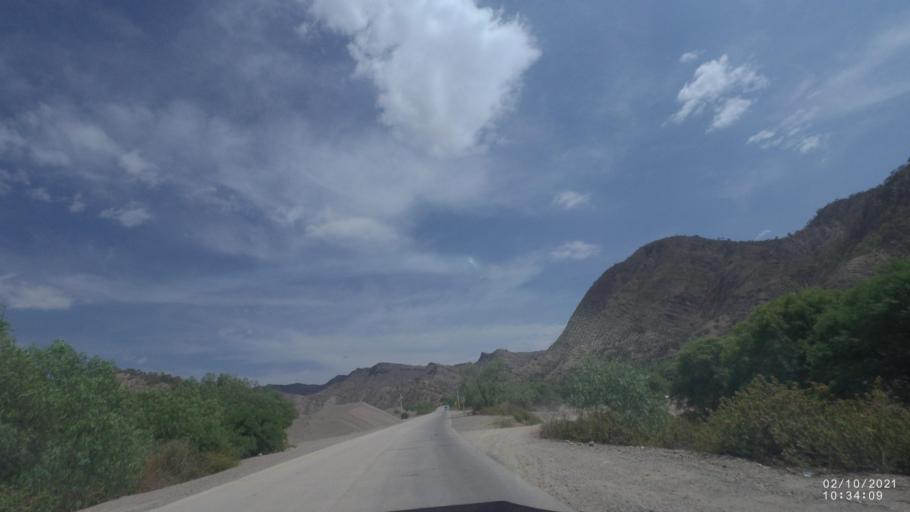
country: BO
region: Cochabamba
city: Capinota
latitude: -17.6756
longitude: -66.2519
